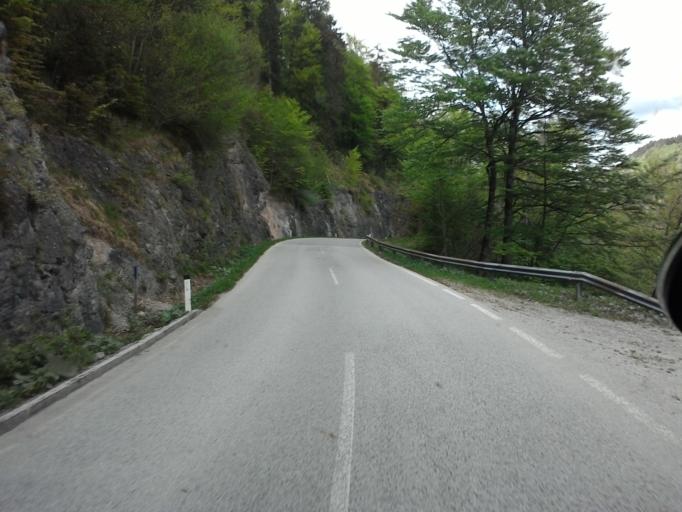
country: AT
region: Styria
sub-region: Politischer Bezirk Liezen
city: Gams bei Hieflau
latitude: 47.6855
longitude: 14.7710
